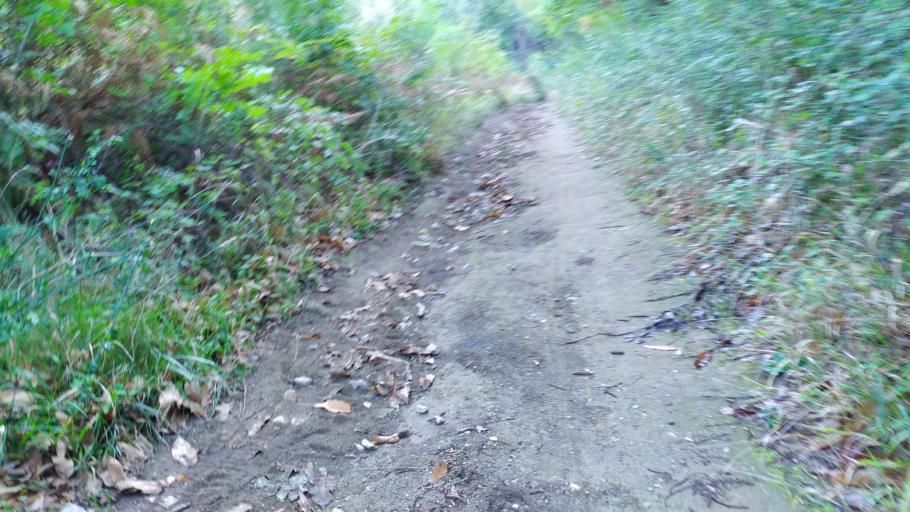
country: IT
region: Campania
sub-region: Provincia di Salerno
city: Lanzara
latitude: 40.7929
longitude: 14.6645
